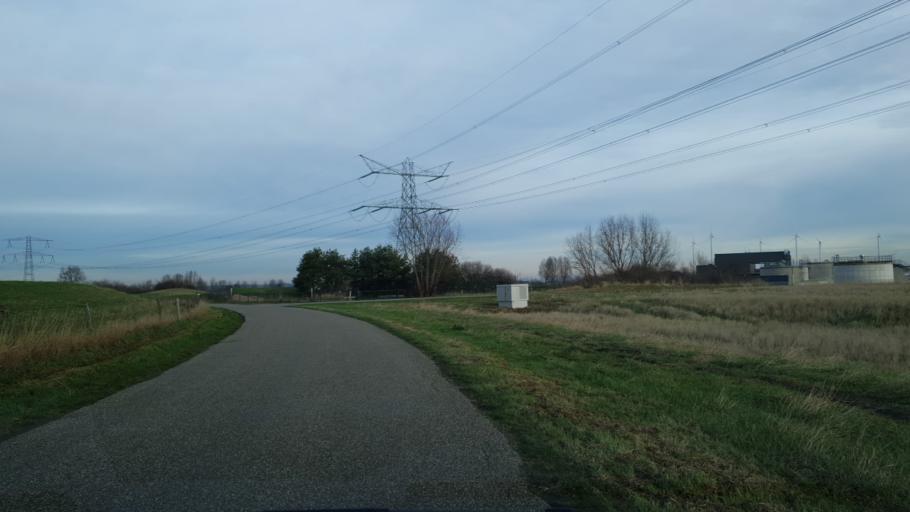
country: NL
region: North Brabant
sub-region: Gemeente Woensdrecht
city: Woensdrecht
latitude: 51.3768
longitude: 4.2475
